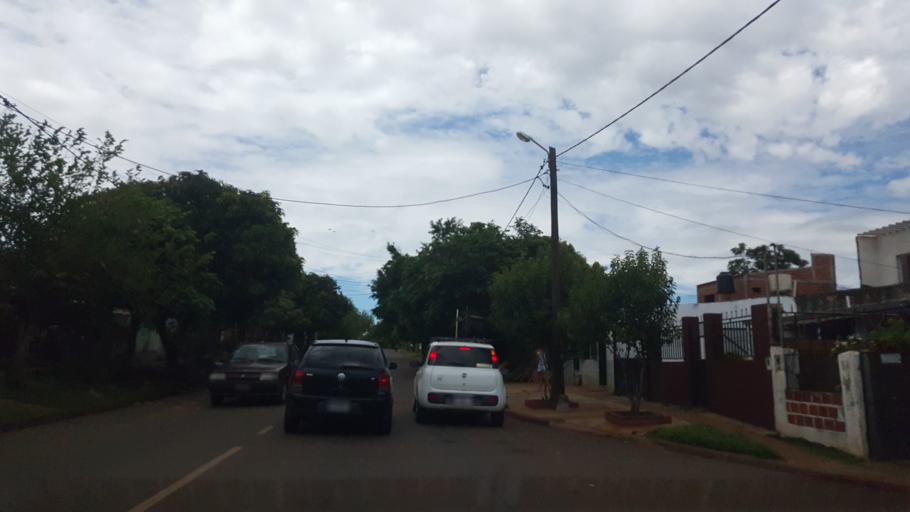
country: AR
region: Misiones
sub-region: Departamento de Capital
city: Posadas
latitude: -27.4194
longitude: -55.8861
